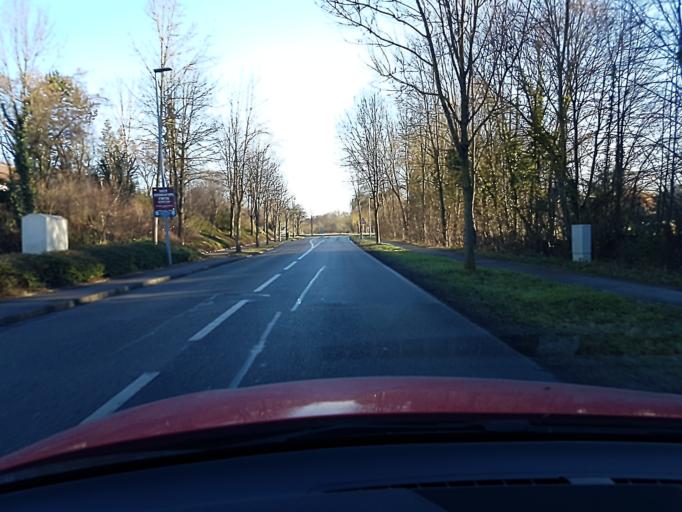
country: DE
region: Baden-Wuerttemberg
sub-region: Regierungsbezirk Stuttgart
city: Freudental
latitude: 49.0092
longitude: 9.0654
